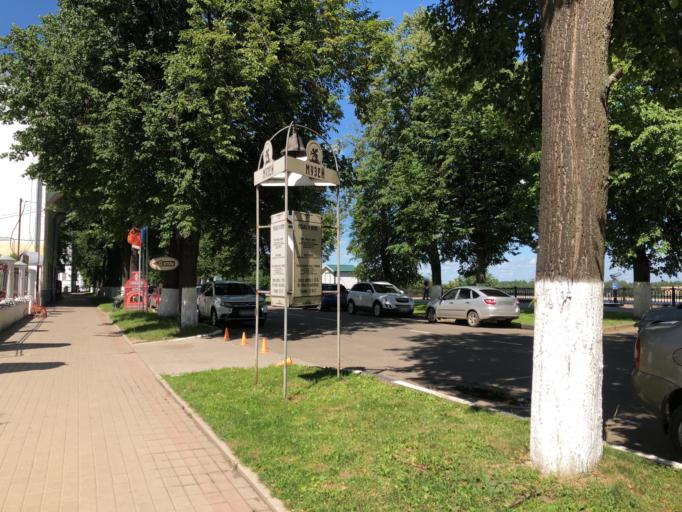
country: RU
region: Jaroslavl
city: Yaroslavl
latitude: 57.6301
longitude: 39.8955
